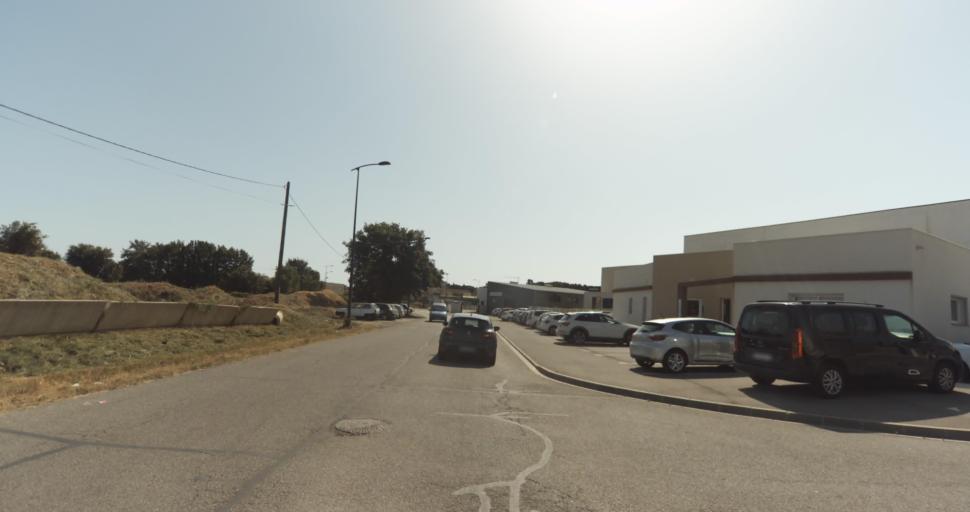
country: FR
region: Languedoc-Roussillon
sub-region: Departement des Pyrenees-Orientales
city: Latour-Bas-Elne
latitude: 42.6139
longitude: 2.9922
